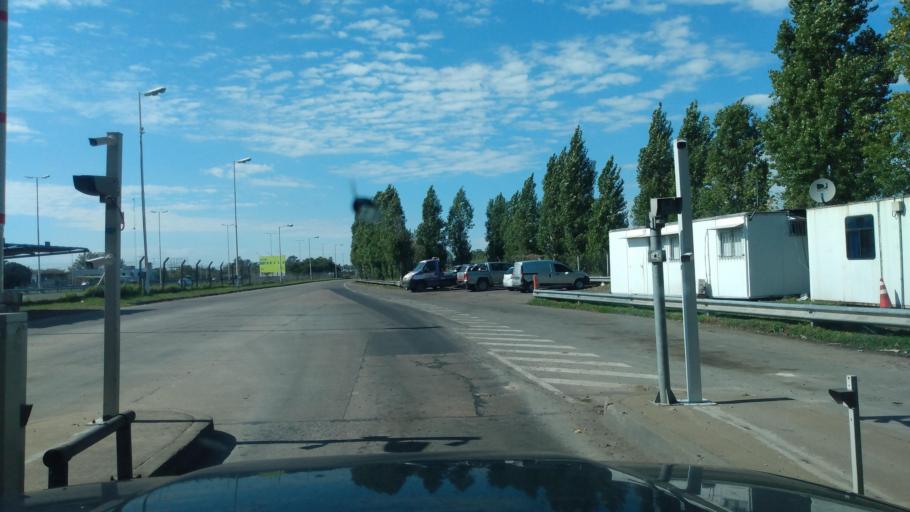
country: AR
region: Buenos Aires
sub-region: Partido de Merlo
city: Merlo
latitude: -34.6286
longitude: -58.7294
